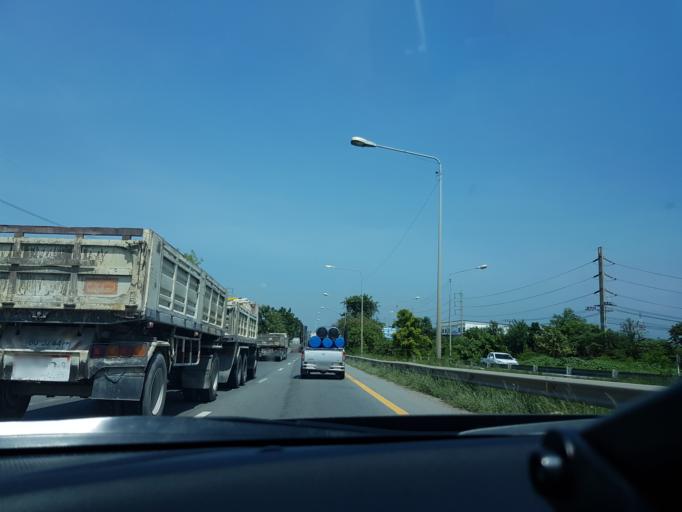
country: TH
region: Sara Buri
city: Saraburi
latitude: 14.5261
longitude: 100.8878
